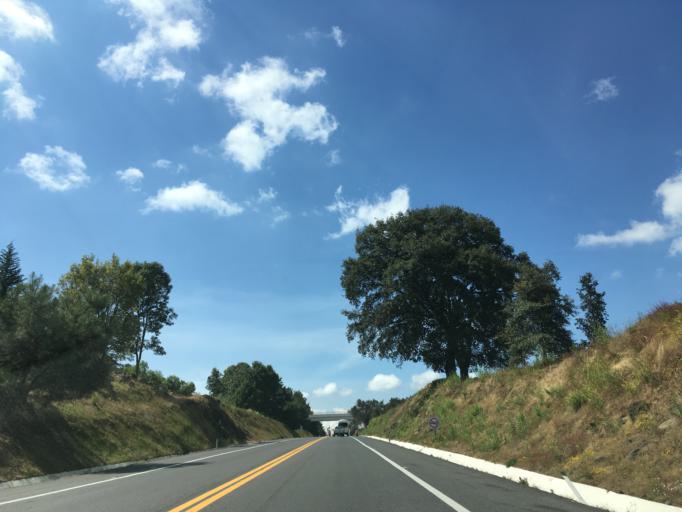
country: MX
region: Michoacan
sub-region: Patzcuaro
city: Santa Ana Chapitiro
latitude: 19.5022
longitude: -101.6422
